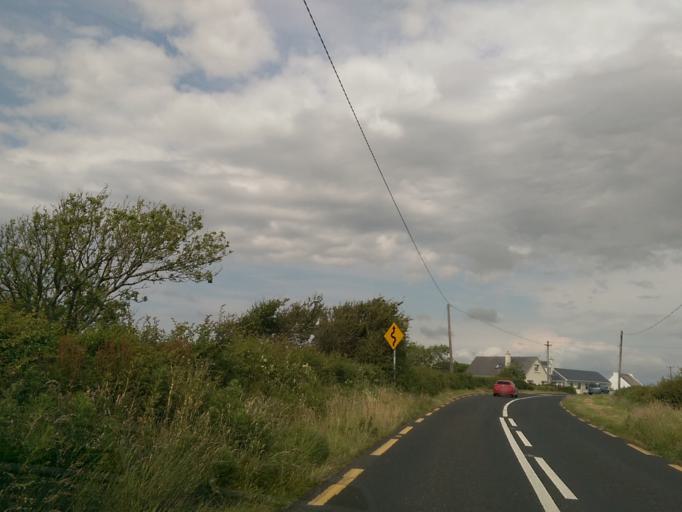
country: IE
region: Munster
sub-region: An Clar
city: Kilrush
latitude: 52.7671
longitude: -9.4518
